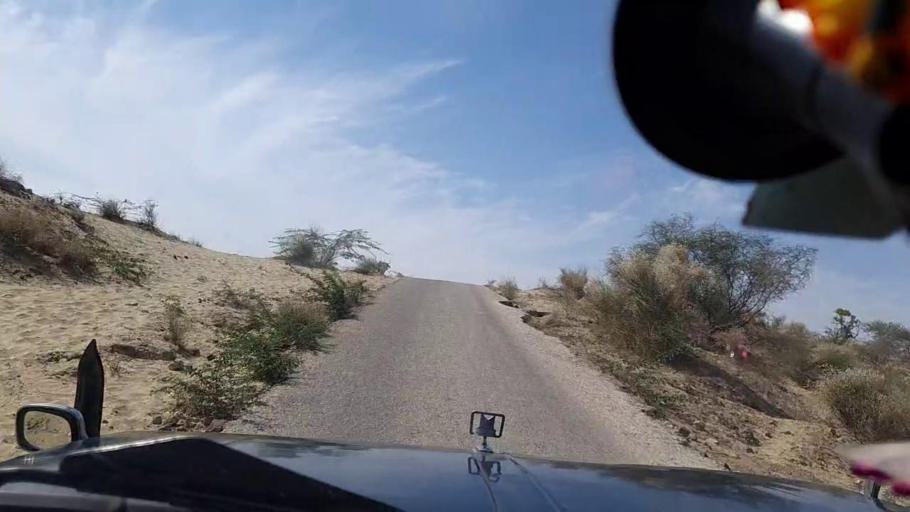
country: PK
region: Sindh
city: Diplo
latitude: 24.4108
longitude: 69.5852
